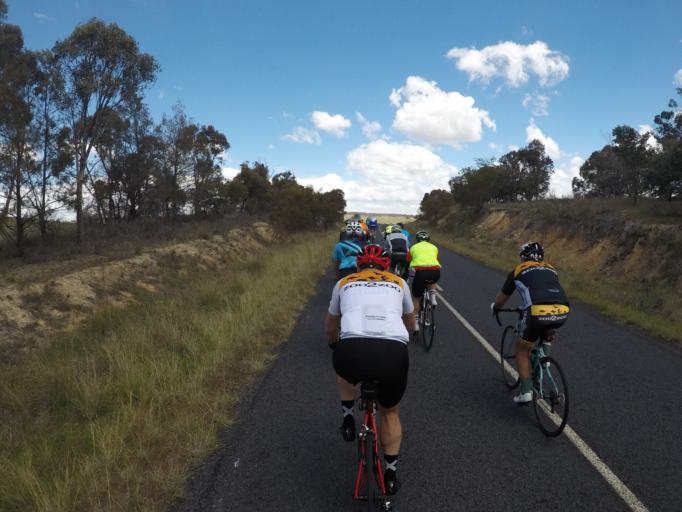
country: AU
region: New South Wales
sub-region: Bathurst Regional
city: Perthville
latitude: -33.5661
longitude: 149.4151
